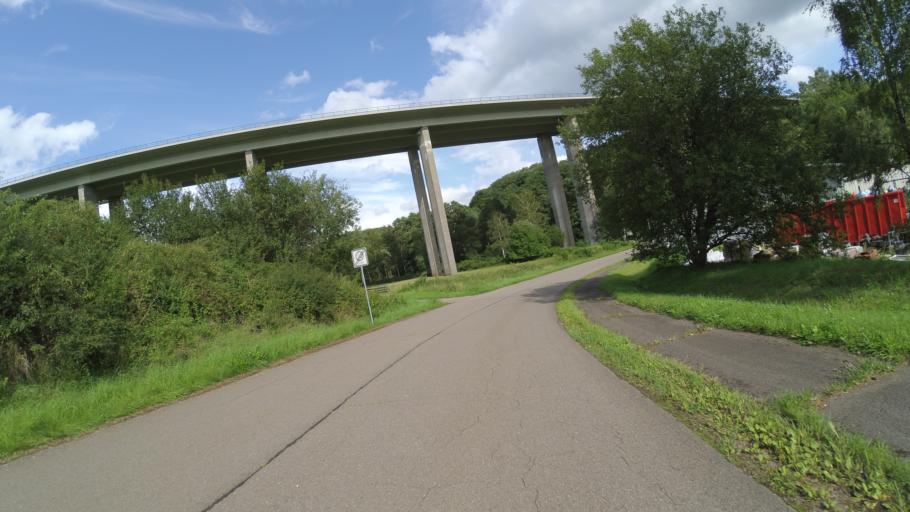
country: DE
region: Saarland
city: Tholey
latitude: 49.5412
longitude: 6.9930
